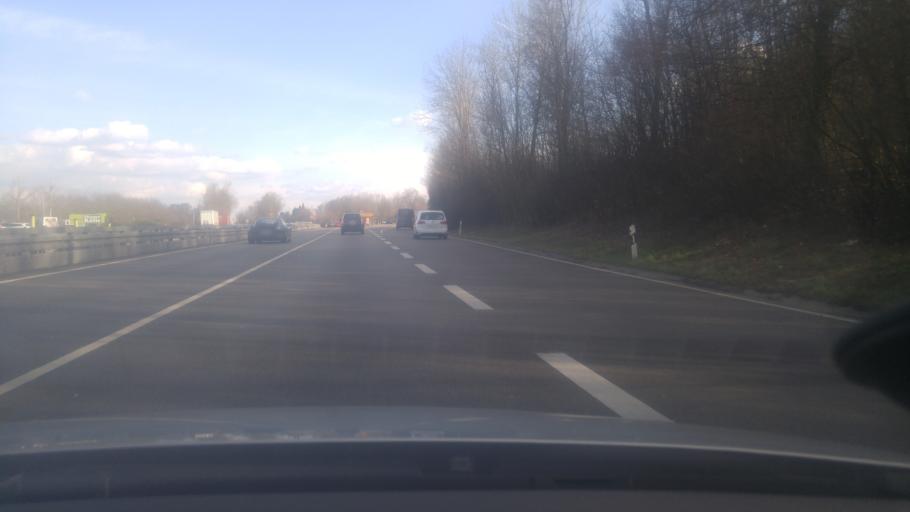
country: DE
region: Baden-Wuerttemberg
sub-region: Regierungsbezirk Stuttgart
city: Korntal
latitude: 48.8430
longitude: 9.1350
